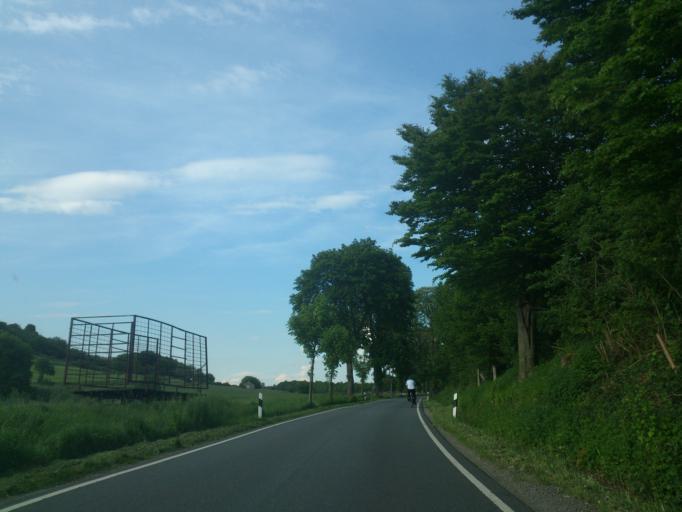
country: DE
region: North Rhine-Westphalia
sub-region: Regierungsbezirk Detmold
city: Altenbeken
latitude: 51.7197
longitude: 8.9363
